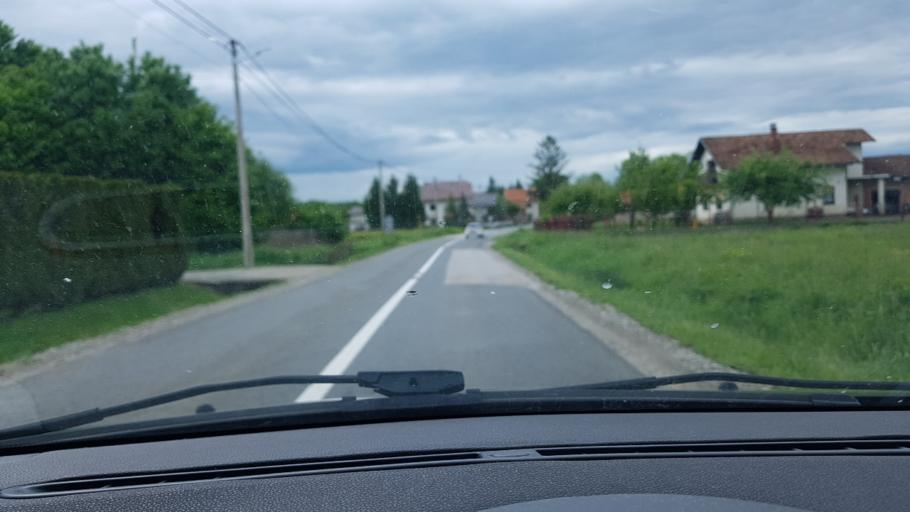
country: HR
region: Krapinsko-Zagorska
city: Oroslavje
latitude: 45.9980
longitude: 15.8852
